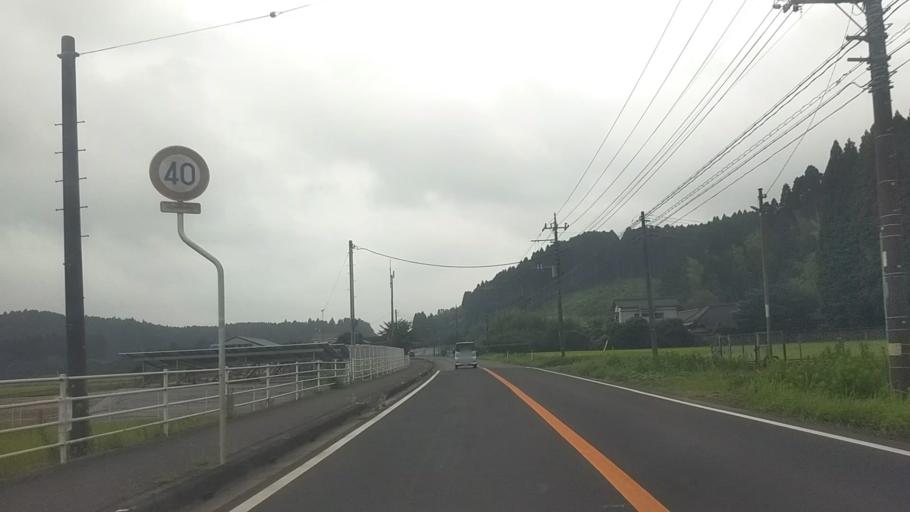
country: JP
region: Chiba
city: Ohara
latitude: 35.2741
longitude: 140.3298
